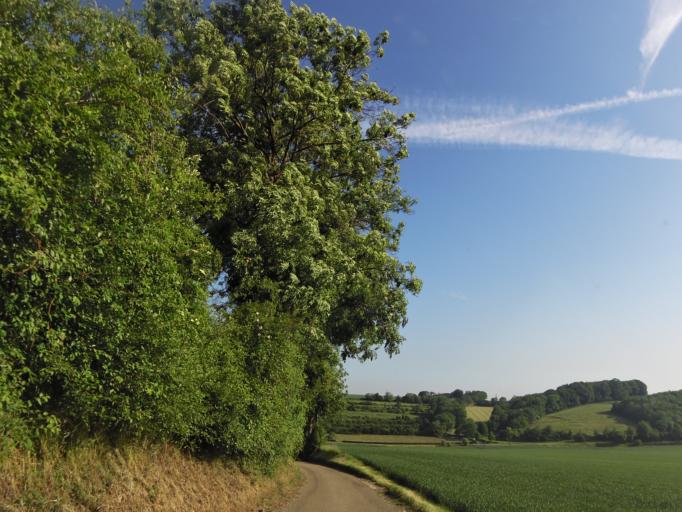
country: NL
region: Limburg
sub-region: Gemeente Voerendaal
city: Ubachsberg
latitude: 50.8447
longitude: 5.9208
